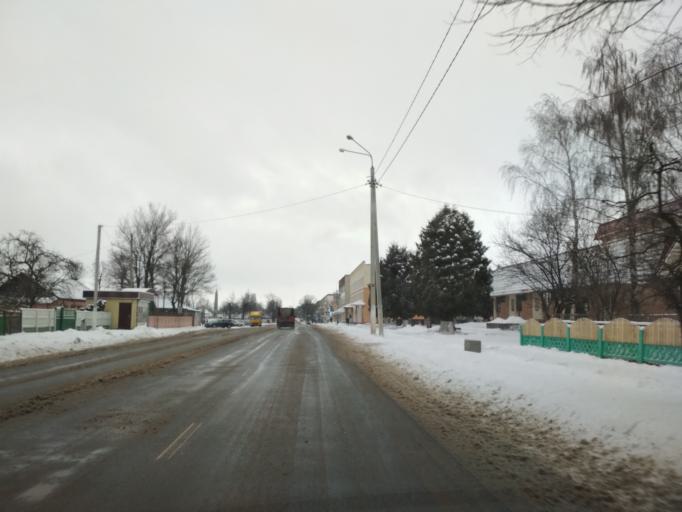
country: BY
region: Minsk
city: Mar''ina Horka
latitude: 53.5090
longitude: 28.1448
